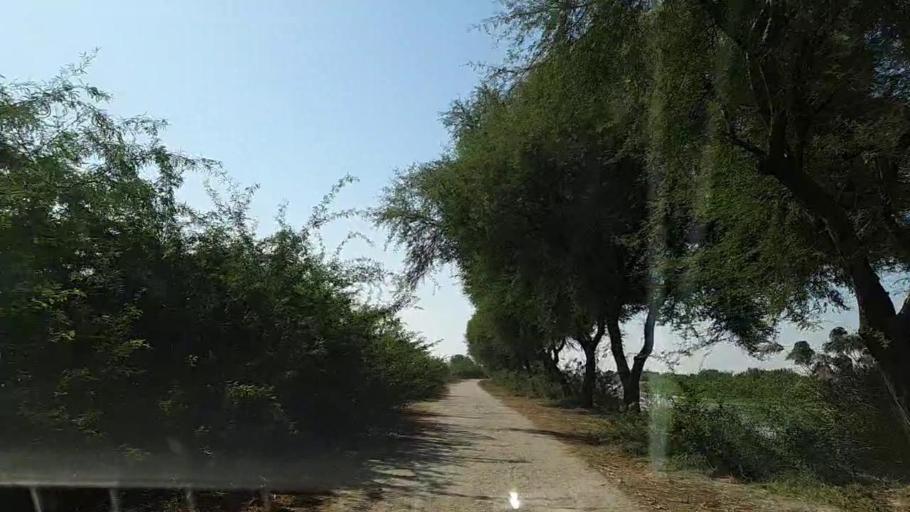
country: PK
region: Sindh
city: Chuhar Jamali
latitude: 24.5806
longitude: 68.0470
